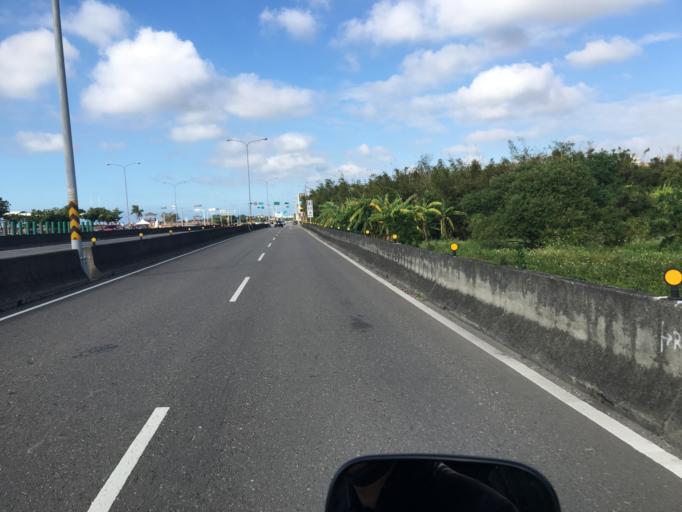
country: TW
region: Taiwan
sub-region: Hsinchu
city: Hsinchu
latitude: 24.7770
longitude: 120.9147
